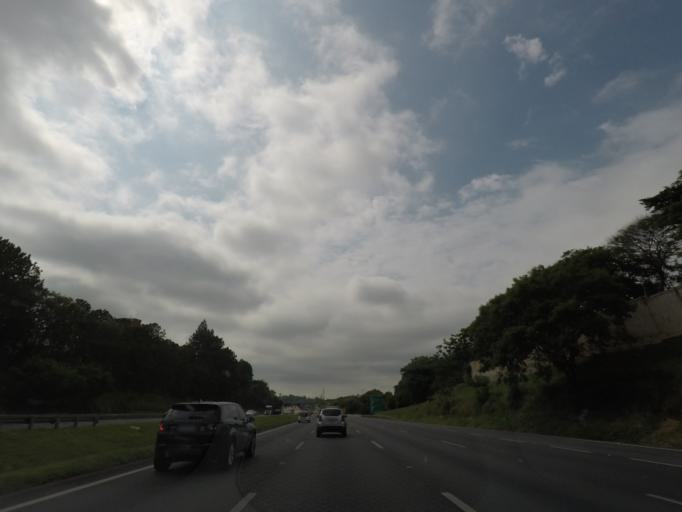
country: BR
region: Sao Paulo
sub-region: Campinas
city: Campinas
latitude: -22.8890
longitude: -47.0114
